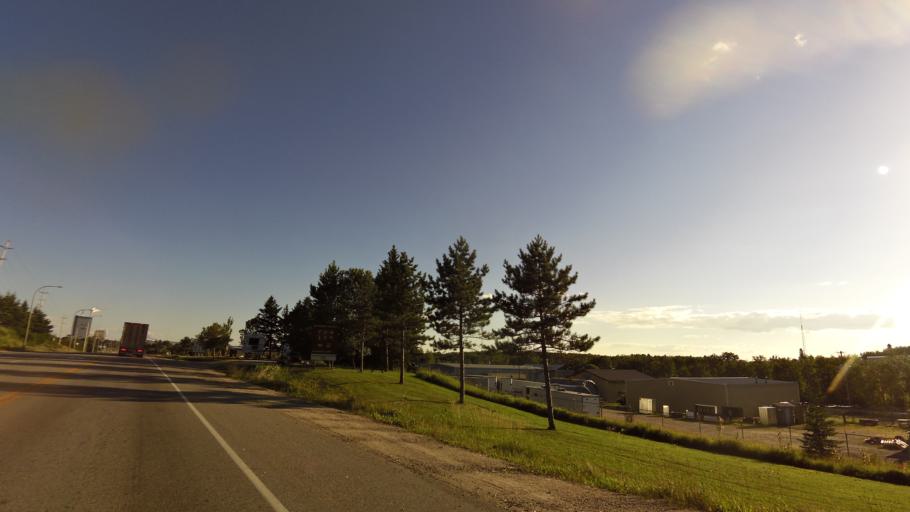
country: CA
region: Ontario
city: Dryden
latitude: 49.8005
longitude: -92.8475
